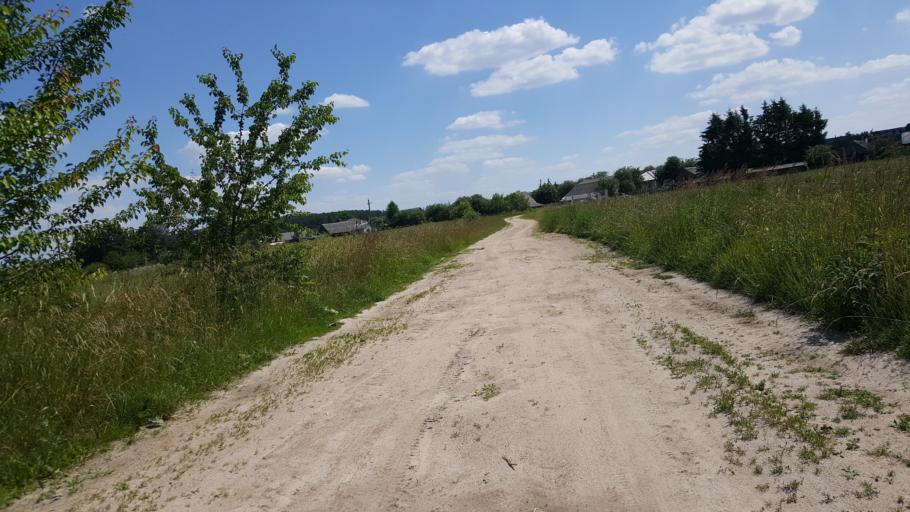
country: BY
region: Brest
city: Kamyanyets
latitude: 52.4101
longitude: 23.8278
